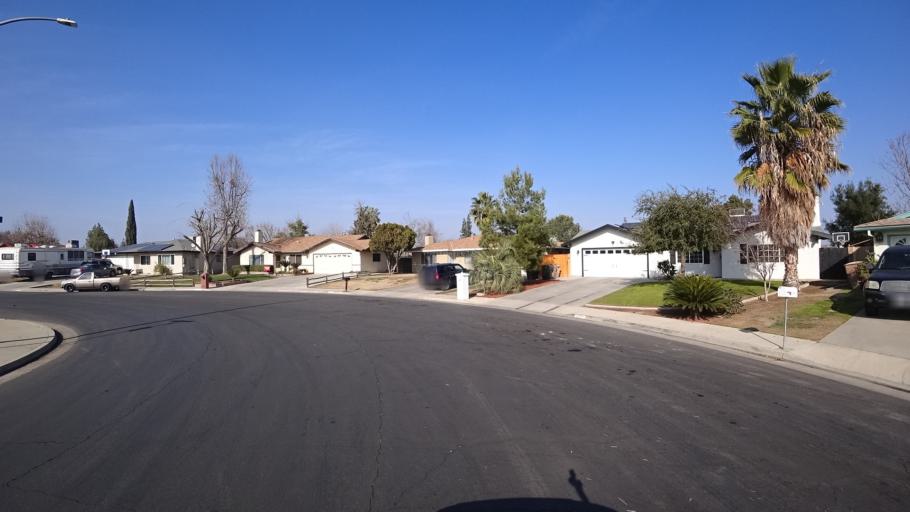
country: US
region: California
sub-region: Kern County
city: Bakersfield
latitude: 35.3282
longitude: -119.0626
